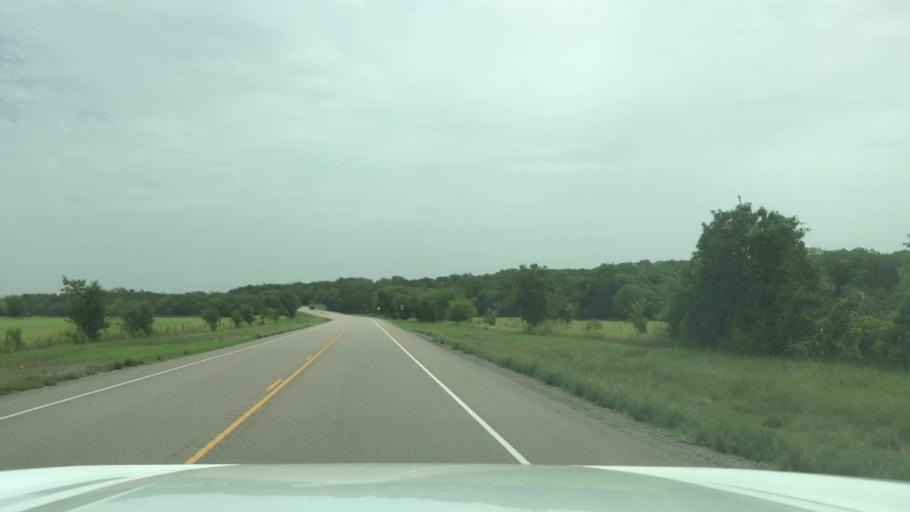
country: US
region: Texas
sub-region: Hamilton County
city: Hico
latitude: 31.9773
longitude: -97.8845
